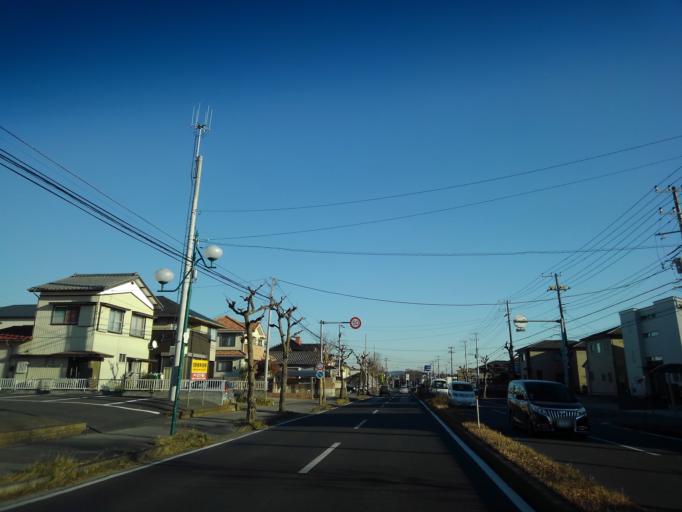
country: JP
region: Chiba
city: Kimitsu
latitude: 35.3207
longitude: 139.9145
